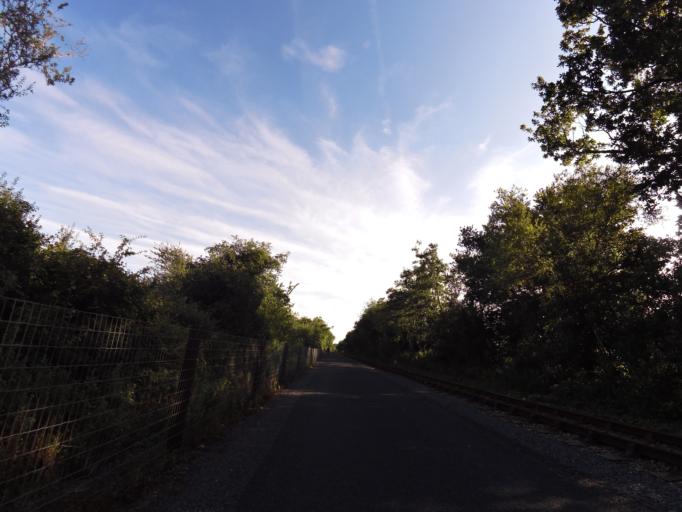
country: IE
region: Leinster
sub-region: Kilkenny
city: Mooncoin
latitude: 52.2534
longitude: -7.1928
